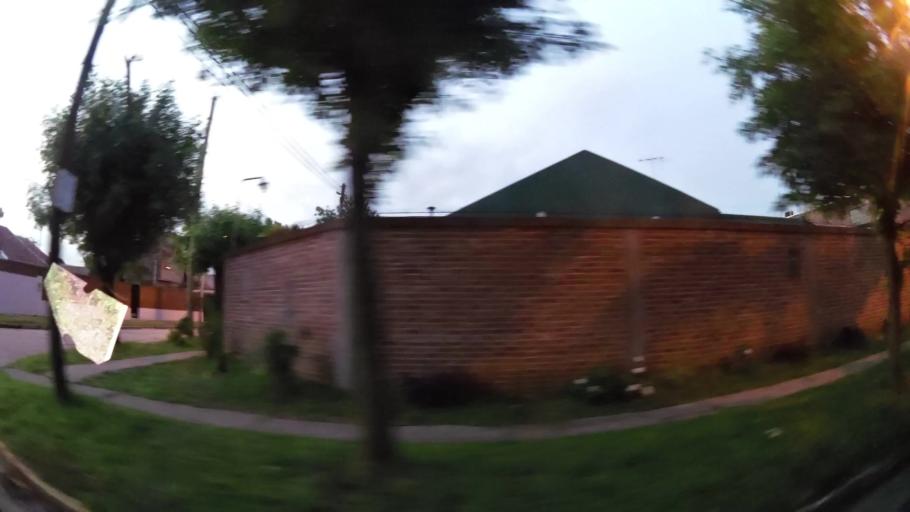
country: AR
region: Buenos Aires
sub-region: Partido de Lomas de Zamora
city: Lomas de Zamora
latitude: -34.7493
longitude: -58.3677
